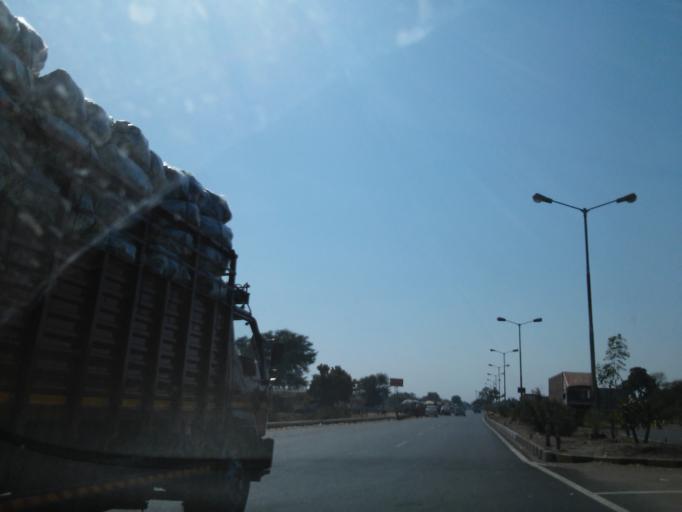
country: IN
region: Gujarat
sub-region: Gandhinagar
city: Chhala
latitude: 23.4096
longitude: 72.8282
